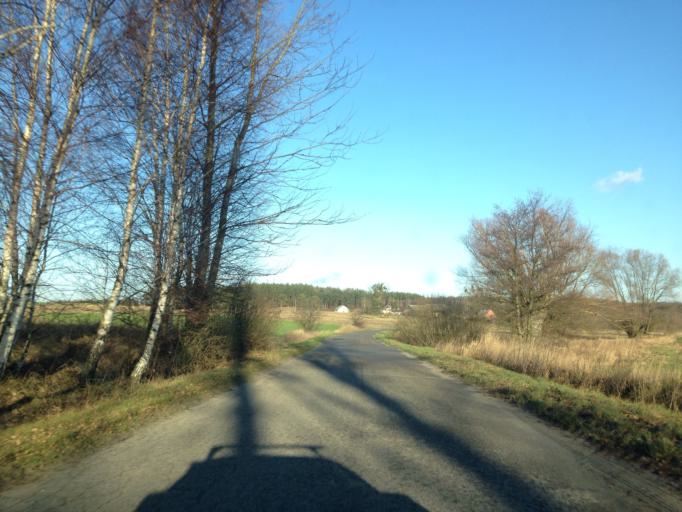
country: PL
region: Pomeranian Voivodeship
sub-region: Powiat kwidzynski
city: Gardeja
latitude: 53.6110
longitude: 19.0340
